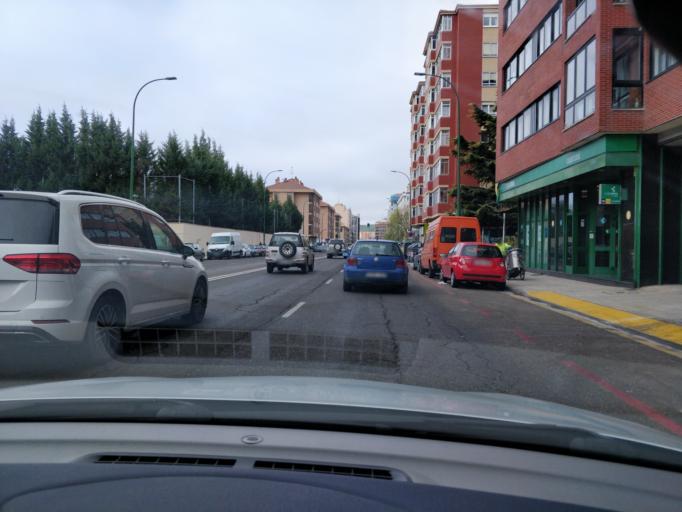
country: ES
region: Castille and Leon
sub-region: Provincia de Burgos
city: Burgos
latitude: 42.3476
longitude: -3.6689
